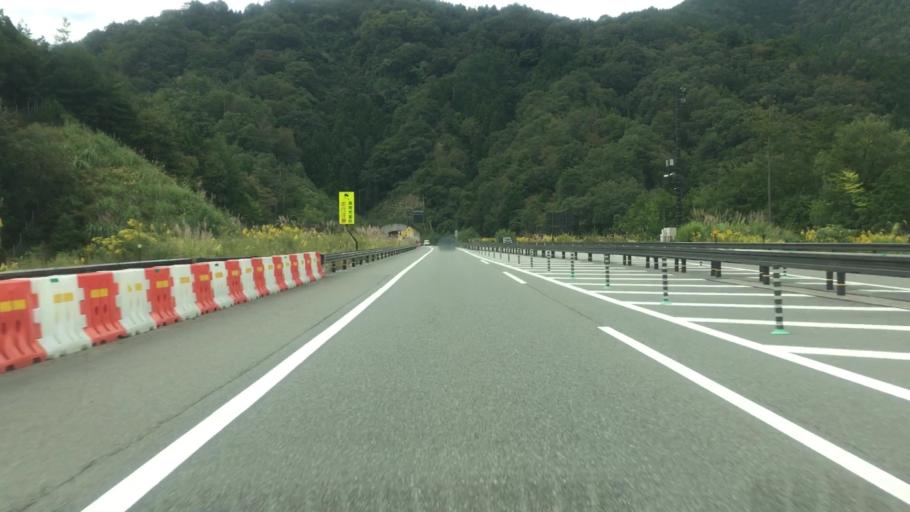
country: JP
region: Hyogo
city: Toyooka
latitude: 35.3440
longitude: 134.8050
